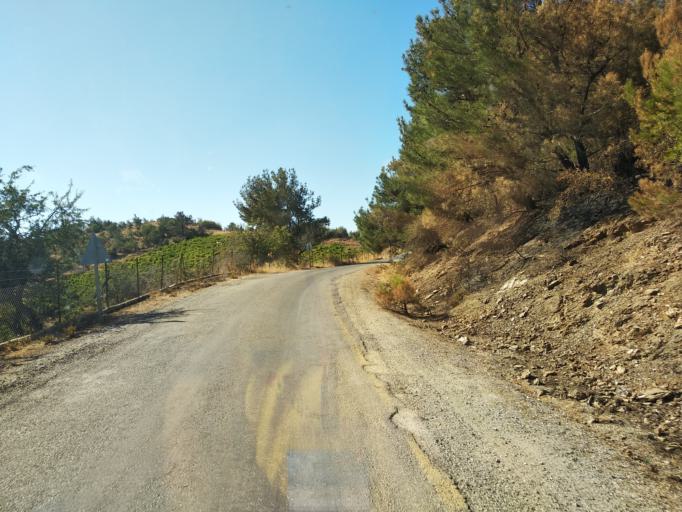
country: TR
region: Izmir
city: Gaziemir
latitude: 38.3061
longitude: 26.9991
